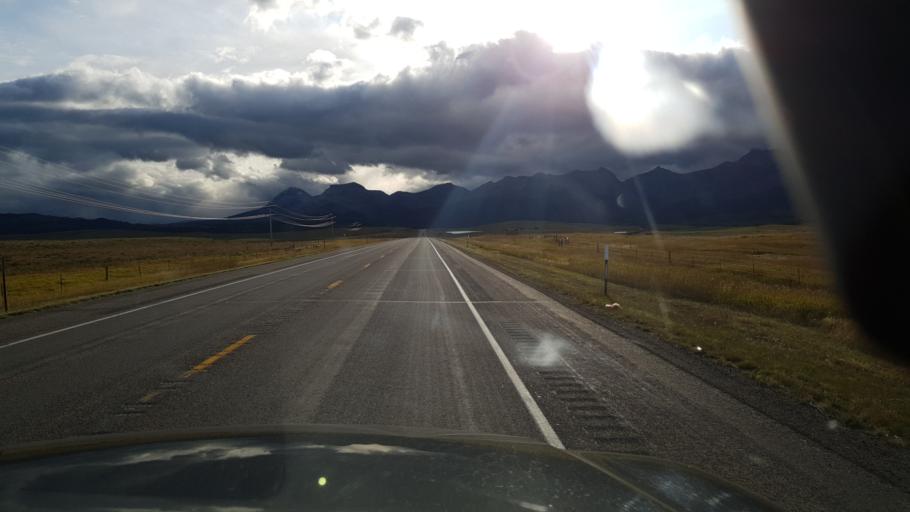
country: US
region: Montana
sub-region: Glacier County
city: South Browning
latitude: 48.4606
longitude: -113.1725
